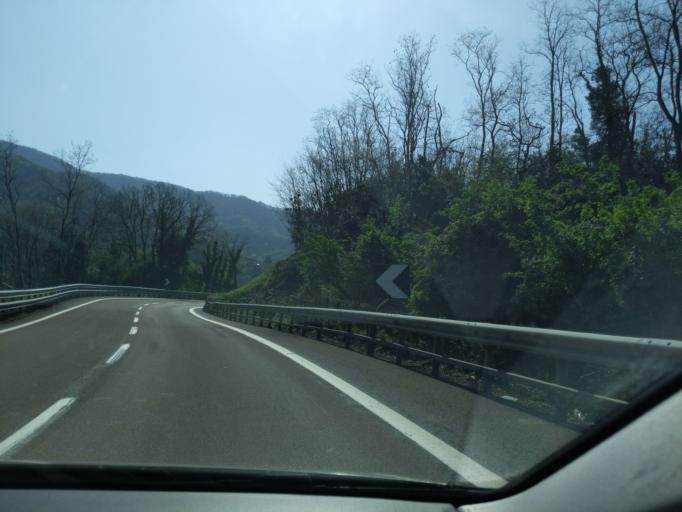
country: IT
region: Liguria
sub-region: Provincia di Genova
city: Pedemonte
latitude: 44.5026
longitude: 8.9209
